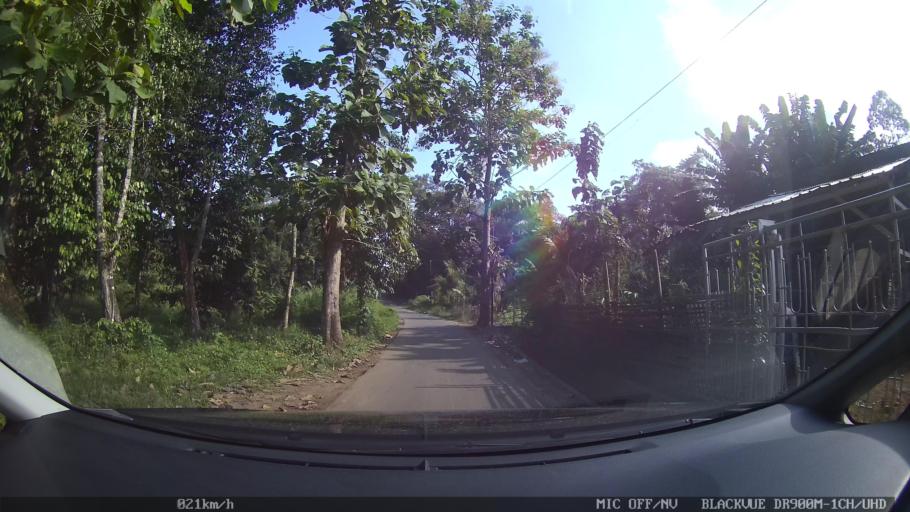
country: ID
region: Lampung
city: Kedaton
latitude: -5.3764
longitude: 105.2335
